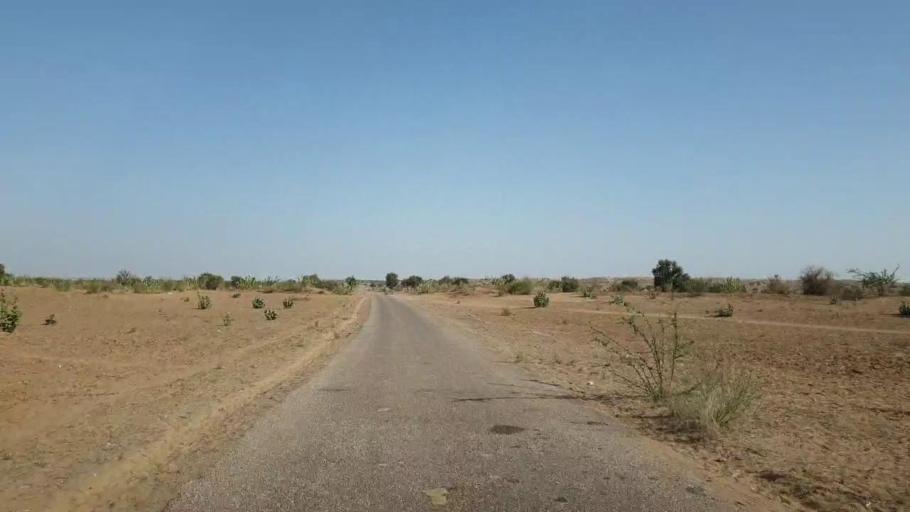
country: PK
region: Sindh
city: Islamkot
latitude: 25.0349
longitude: 70.0304
